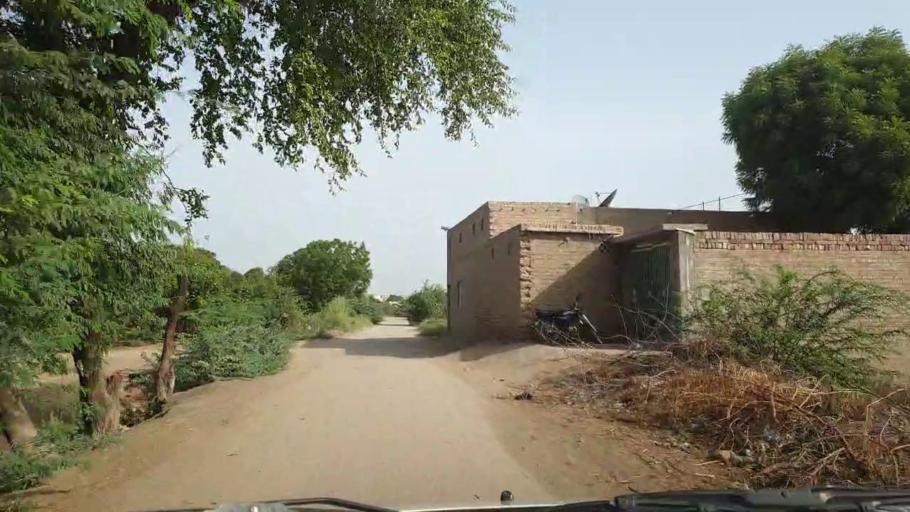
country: PK
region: Sindh
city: Nawabshah
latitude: 26.2306
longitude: 68.4098
